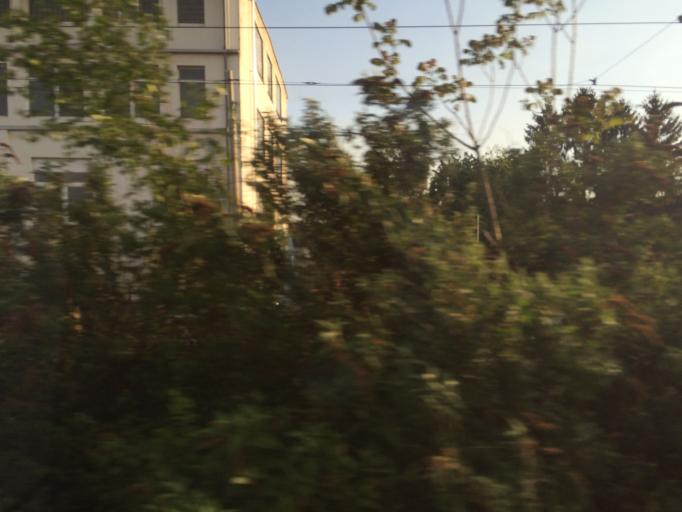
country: DE
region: North Rhine-Westphalia
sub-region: Regierungsbezirk Dusseldorf
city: Muelheim (Ruhr)
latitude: 51.4475
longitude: 6.8577
